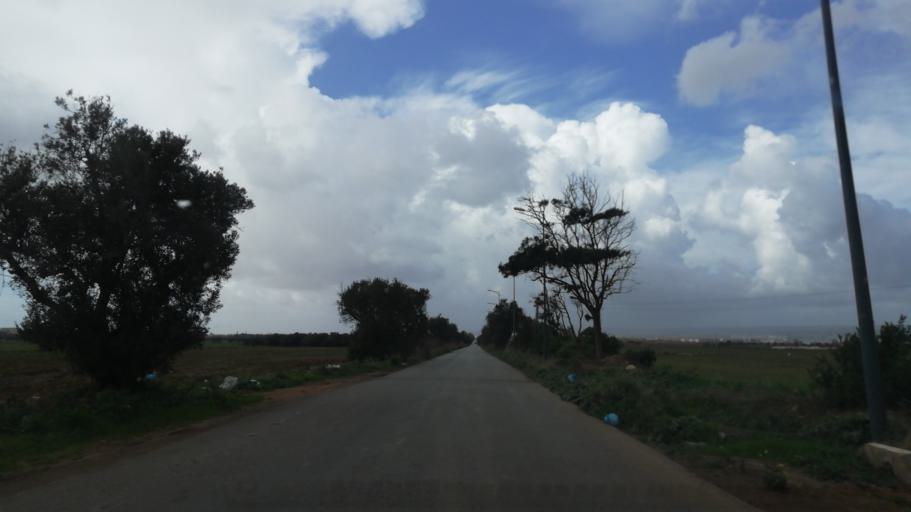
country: DZ
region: Oran
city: Sidi ech Chahmi
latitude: 35.6227
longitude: -0.5521
